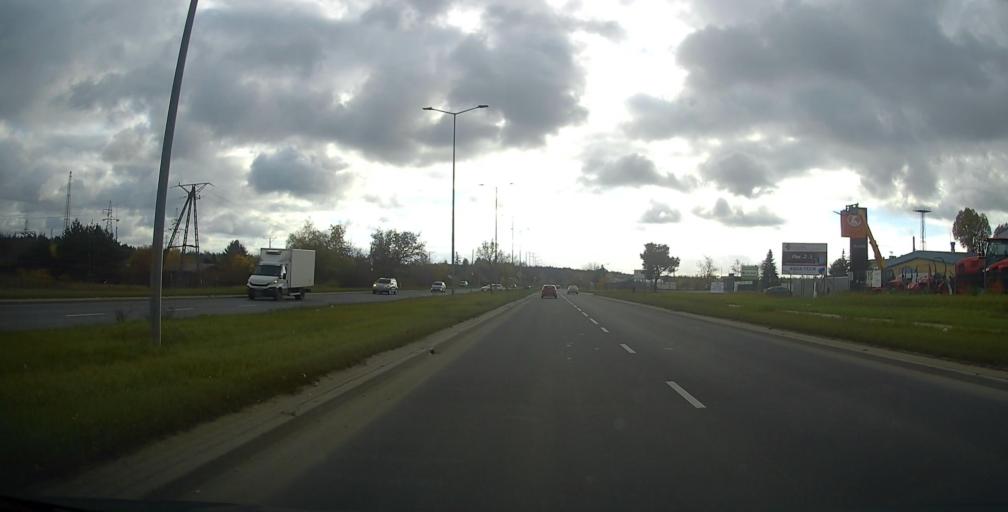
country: PL
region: Warmian-Masurian Voivodeship
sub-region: Powiat elcki
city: Elk
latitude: 53.8265
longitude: 22.3912
